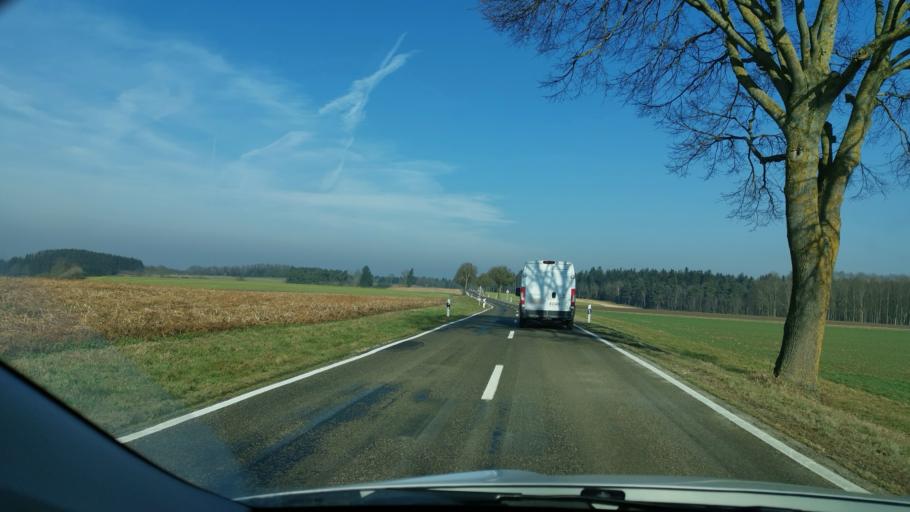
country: DE
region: Bavaria
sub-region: Swabia
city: Holzheim
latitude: 48.6181
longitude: 10.9364
